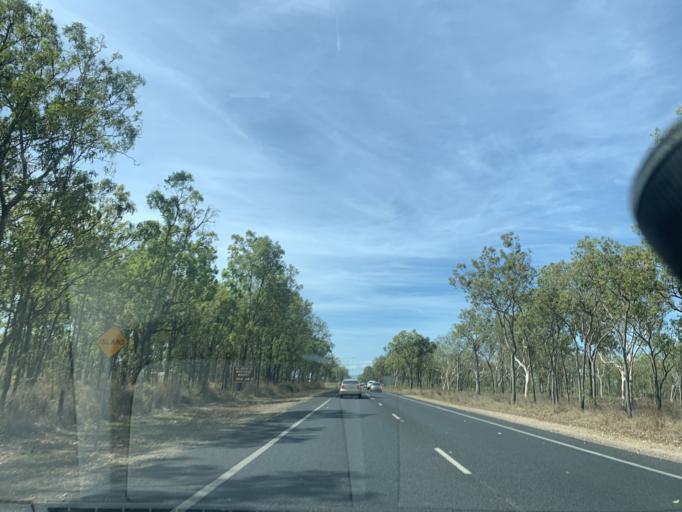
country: AU
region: Queensland
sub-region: Tablelands
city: Mareeba
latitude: -17.0208
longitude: 145.4263
